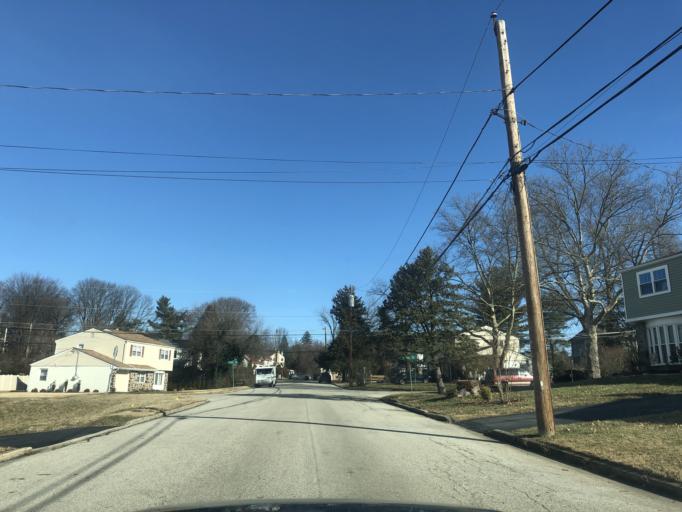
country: US
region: Pennsylvania
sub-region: Montgomery County
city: Plymouth Meeting
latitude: 40.0833
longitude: -75.2561
